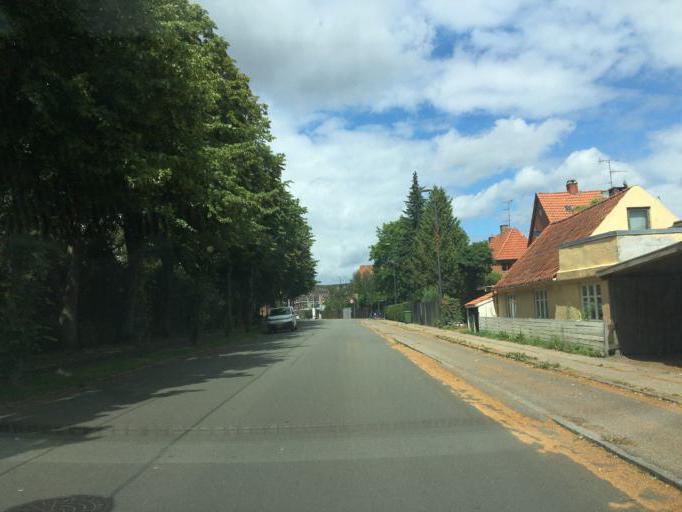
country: DK
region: Capital Region
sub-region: Tarnby Kommune
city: Tarnby
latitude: 55.6510
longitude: 12.6035
